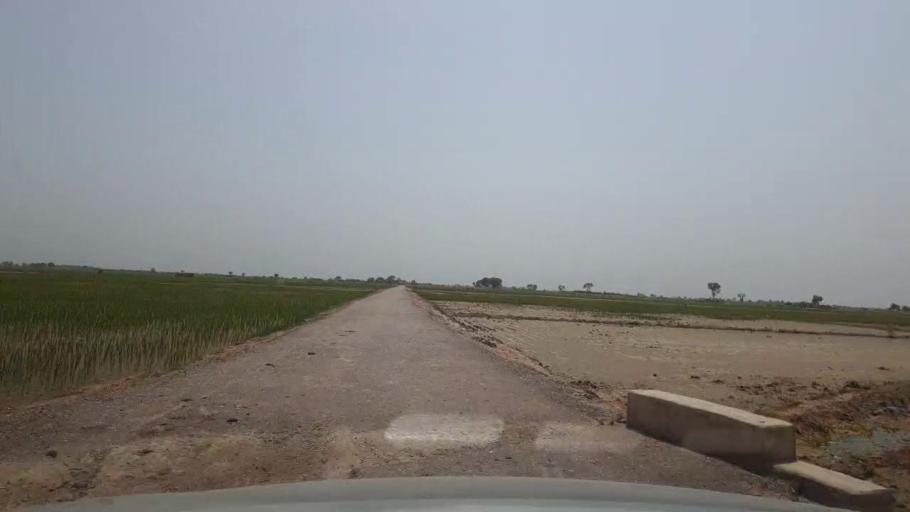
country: PK
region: Sindh
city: Garhi Yasin
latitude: 28.0633
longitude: 68.3190
